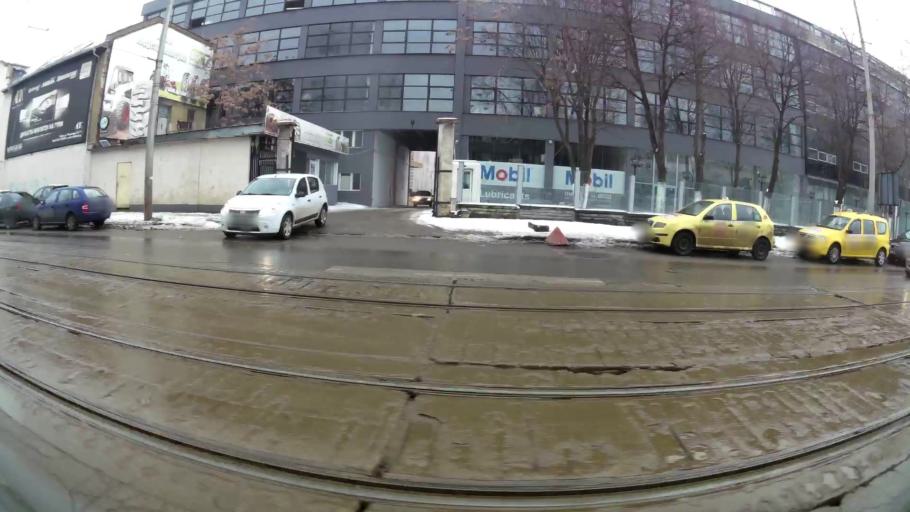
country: BG
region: Sofia-Capital
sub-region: Stolichna Obshtina
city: Sofia
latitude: 42.7093
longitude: 23.3350
